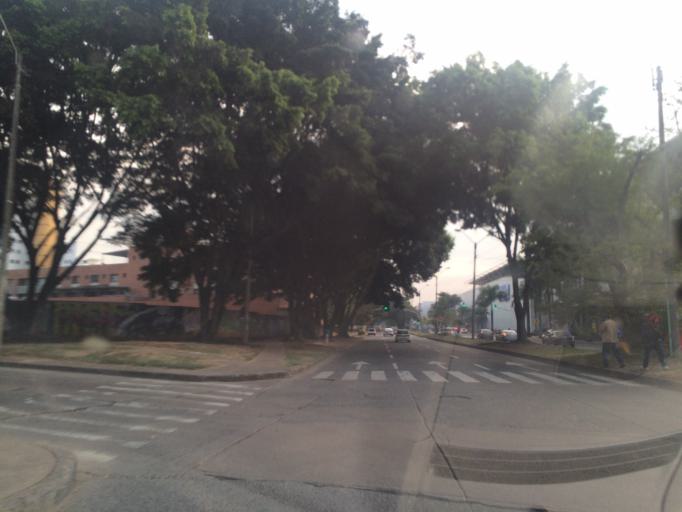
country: CO
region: Valle del Cauca
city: Cali
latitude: 3.4114
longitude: -76.5417
